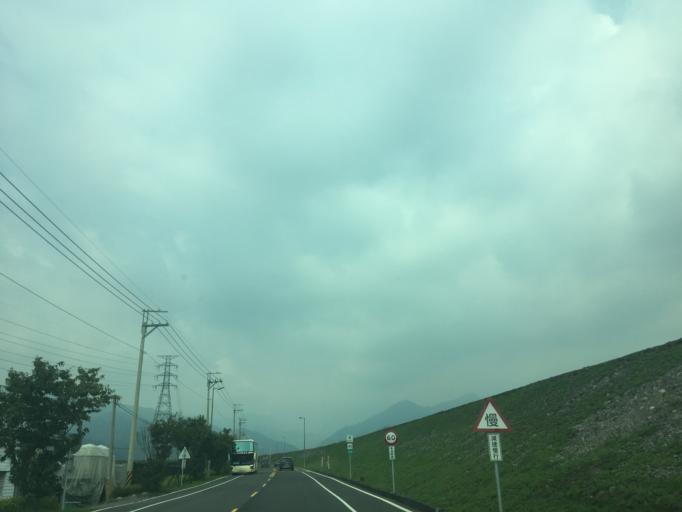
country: TW
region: Taiwan
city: Fengyuan
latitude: 24.2890
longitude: 120.8544
